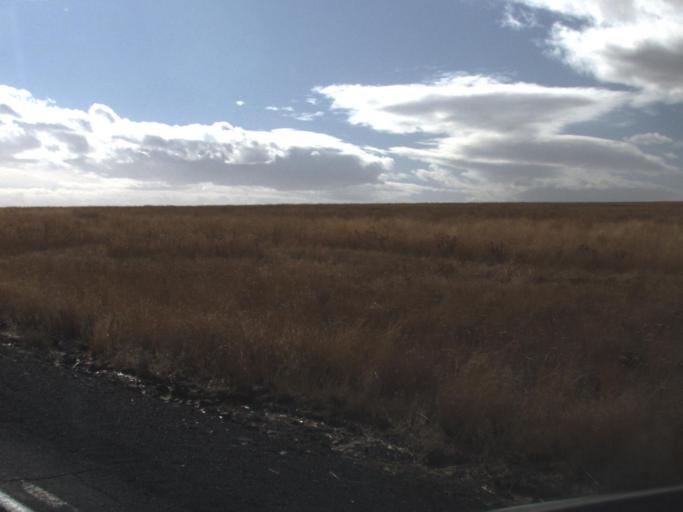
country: US
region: Washington
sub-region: Okanogan County
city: Coulee Dam
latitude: 47.6048
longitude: -118.7861
